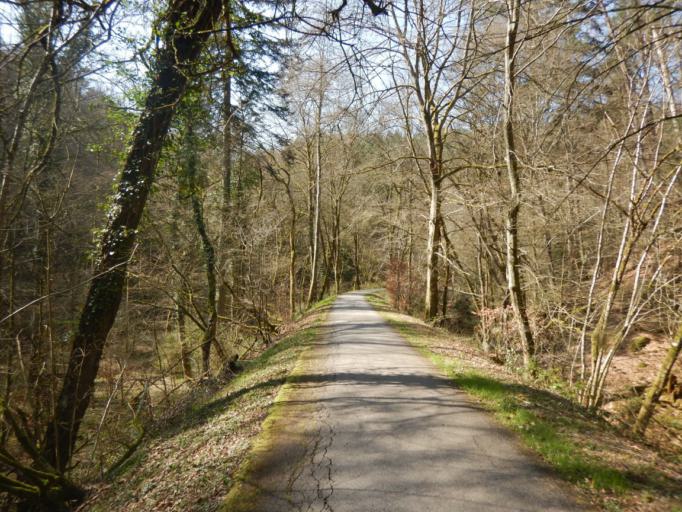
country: LU
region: Grevenmacher
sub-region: Canton d'Echternach
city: Berdorf
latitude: 49.7907
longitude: 6.3617
